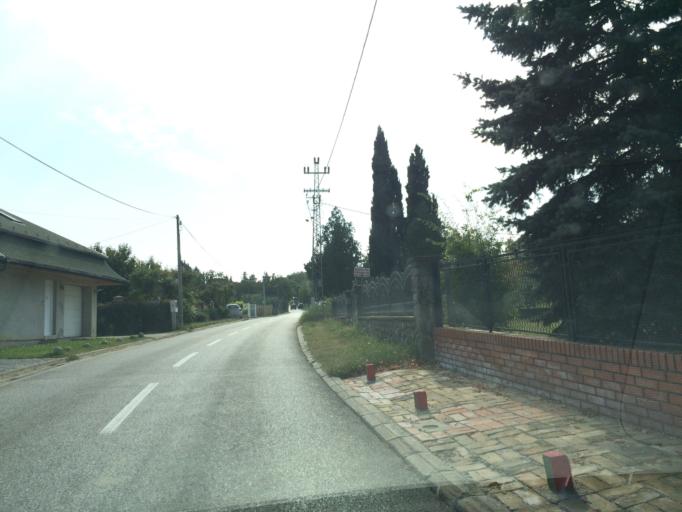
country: RS
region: Autonomna Pokrajina Vojvodina
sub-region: Juznobacki Okrug
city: Novi Sad
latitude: 45.2076
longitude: 19.8336
